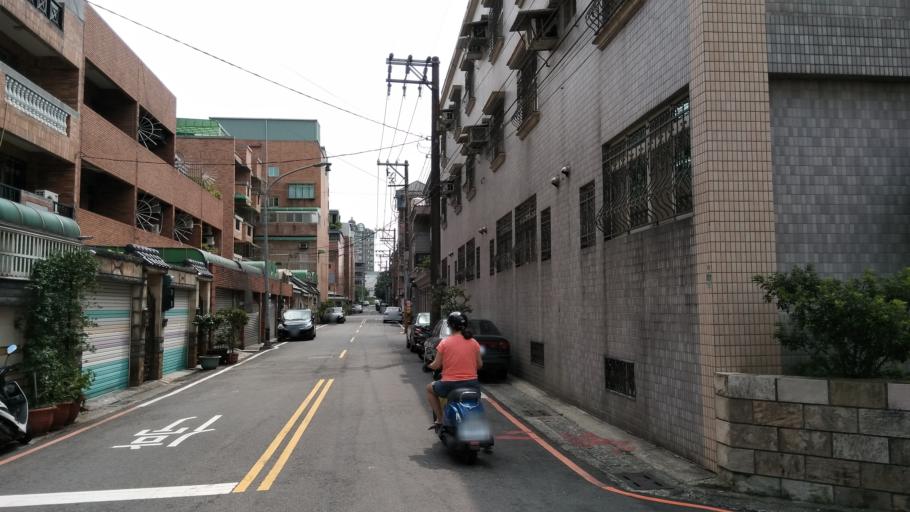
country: TW
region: Taiwan
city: Taoyuan City
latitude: 25.0210
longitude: 121.2654
